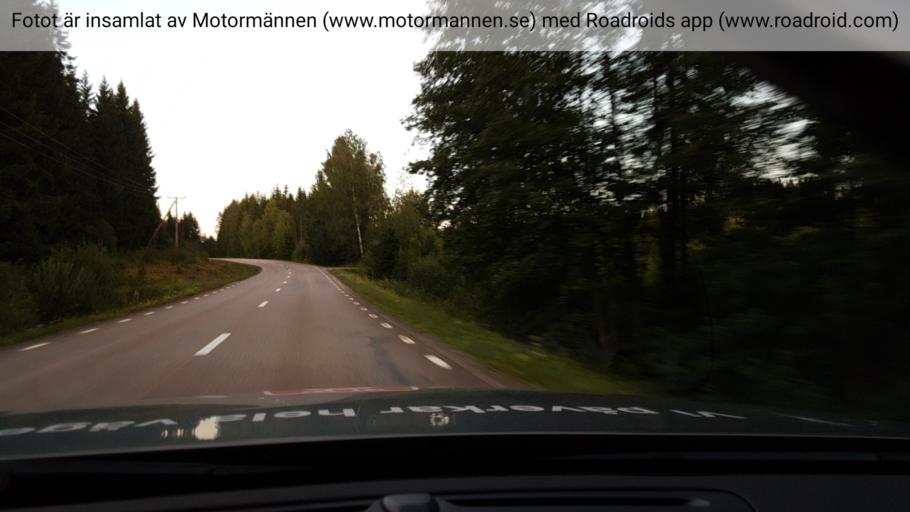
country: SE
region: OErebro
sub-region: Hallefors Kommun
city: Haellefors
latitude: 59.6782
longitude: 14.5004
